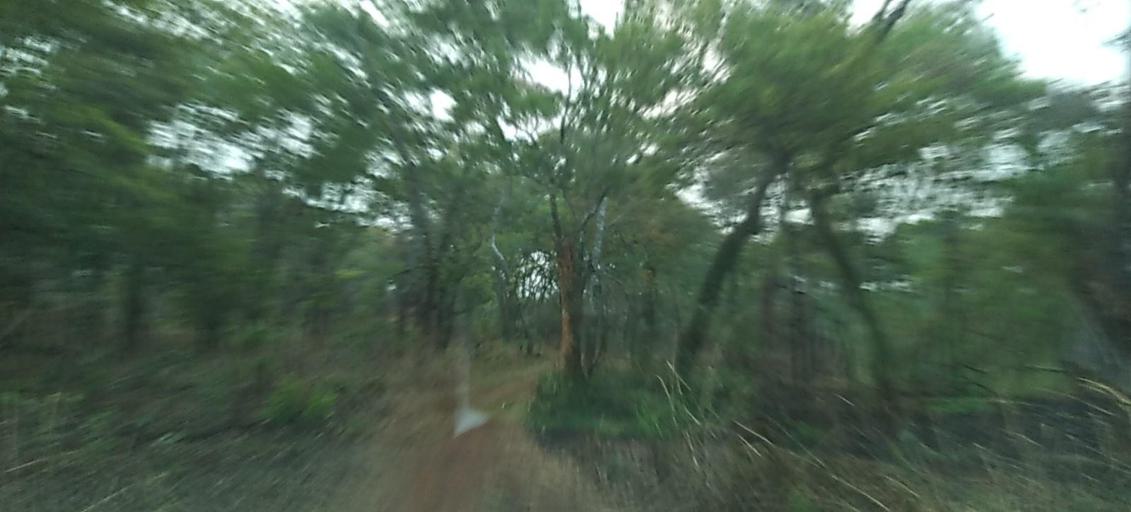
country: ZM
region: North-Western
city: Solwezi
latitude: -12.0447
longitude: 26.0125
